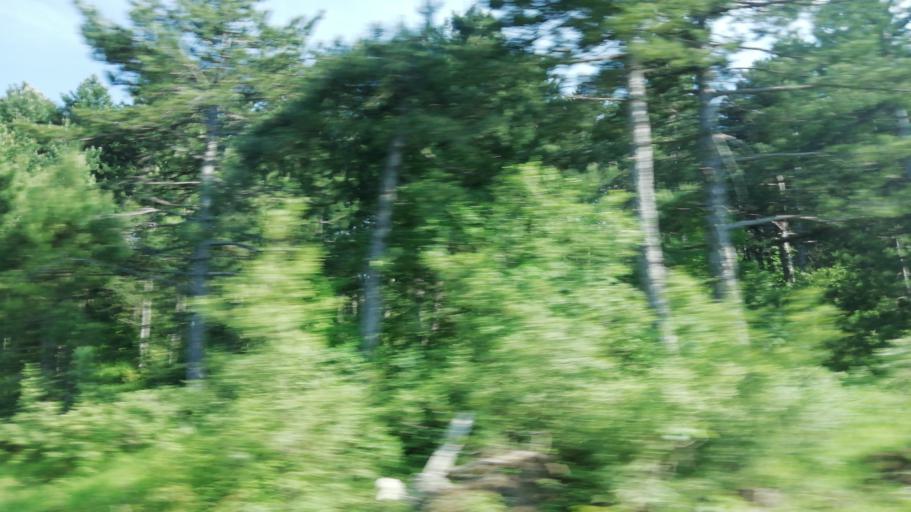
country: TR
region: Karabuk
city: Karabuk
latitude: 41.0868
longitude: 32.5724
